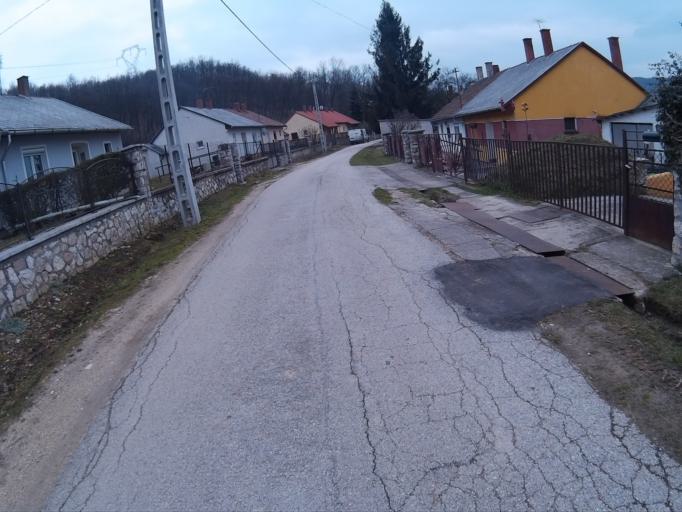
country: HU
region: Veszprem
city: Zirc
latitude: 47.2055
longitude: 17.9229
